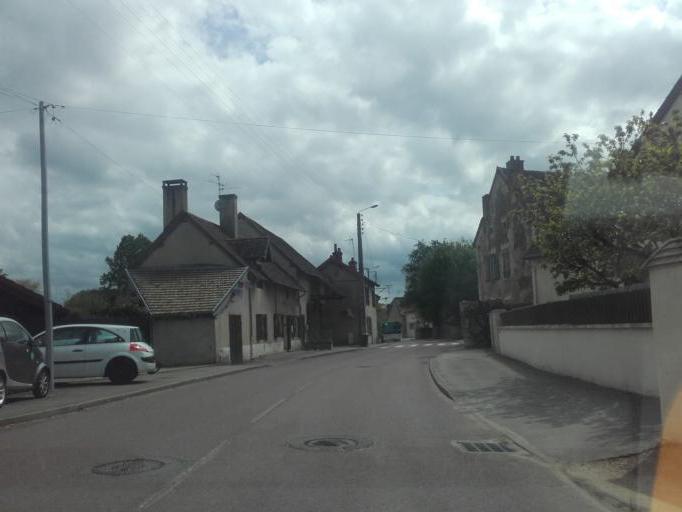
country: FR
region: Bourgogne
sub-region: Departement de Saone-et-Loire
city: Saint-Remy
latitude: 46.7700
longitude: 4.8148
